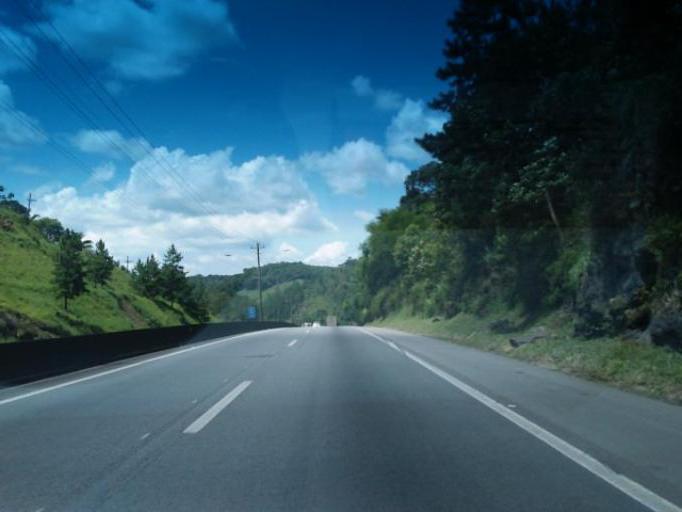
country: BR
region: Sao Paulo
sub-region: Sao Lourenco Da Serra
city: Sao Lourenco da Serra
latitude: -23.9005
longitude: -46.9892
